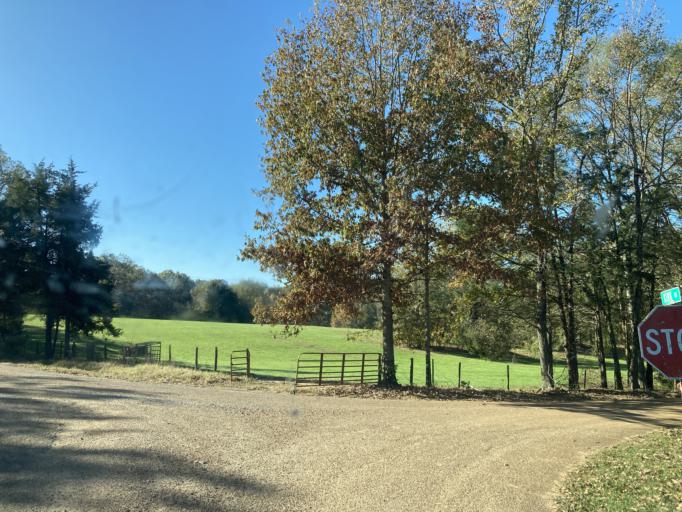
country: US
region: Mississippi
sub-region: Madison County
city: Kearney Park
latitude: 32.7135
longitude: -90.3555
